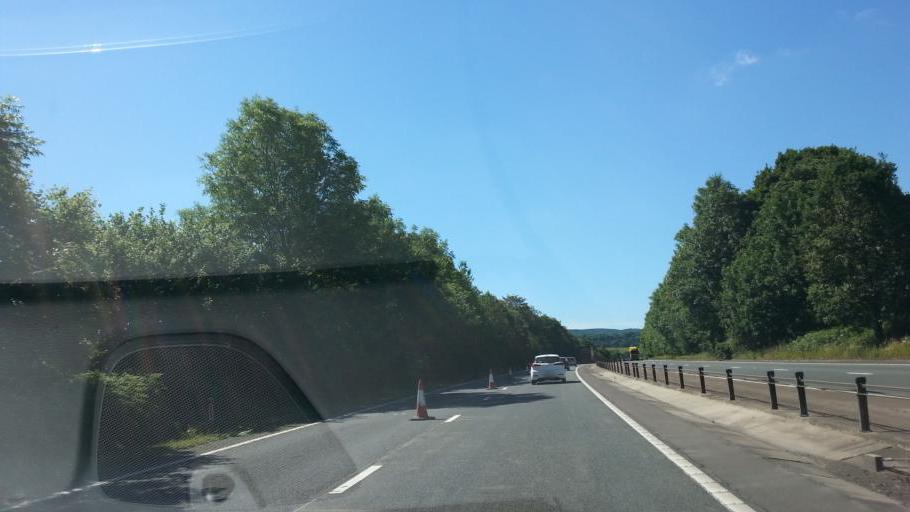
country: GB
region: Wales
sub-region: Monmouthshire
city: Llanbadoc
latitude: 51.6803
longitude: -2.8760
